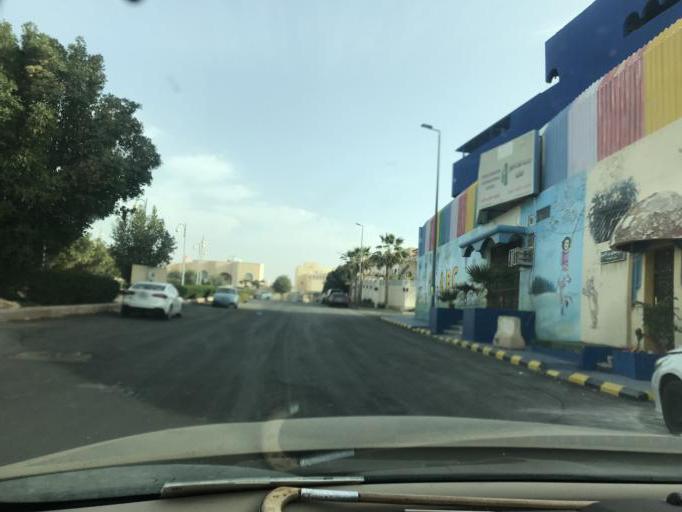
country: SA
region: Ar Riyad
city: Riyadh
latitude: 24.7388
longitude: 46.7515
